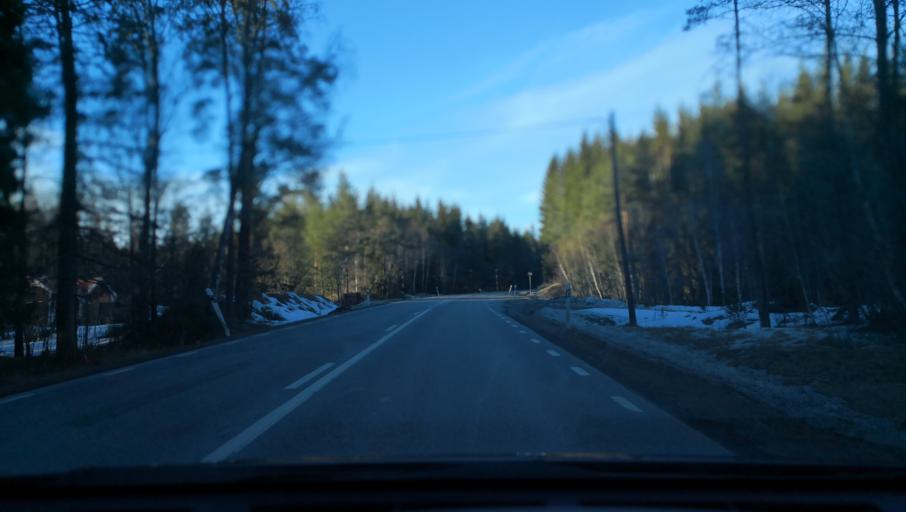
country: SE
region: Uppsala
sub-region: Osthammars Kommun
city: Gimo
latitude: 60.2100
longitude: 18.1919
